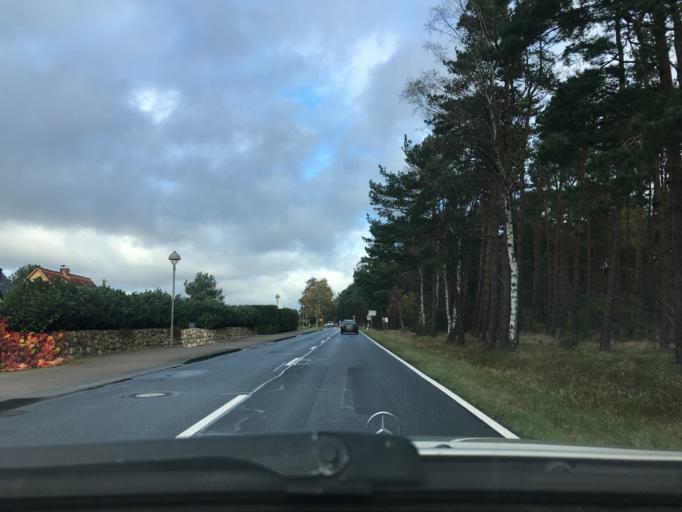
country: DE
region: Mecklenburg-Vorpommern
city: Karlshagen
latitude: 54.0957
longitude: 13.8554
